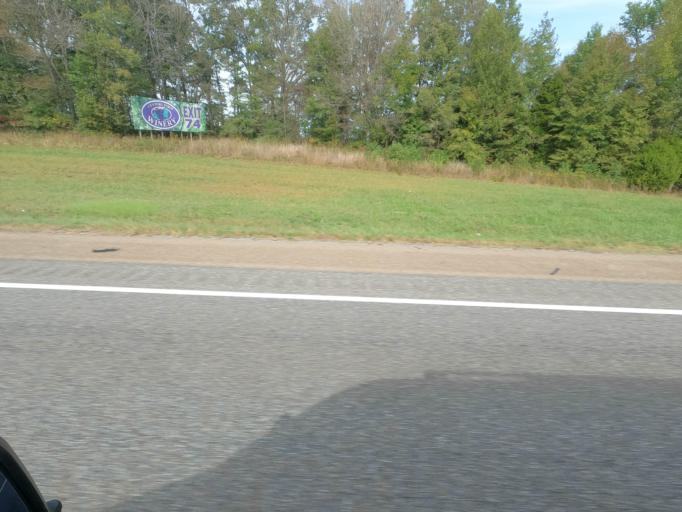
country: US
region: Tennessee
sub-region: Henderson County
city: Lexington
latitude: 35.8004
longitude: -88.3493
